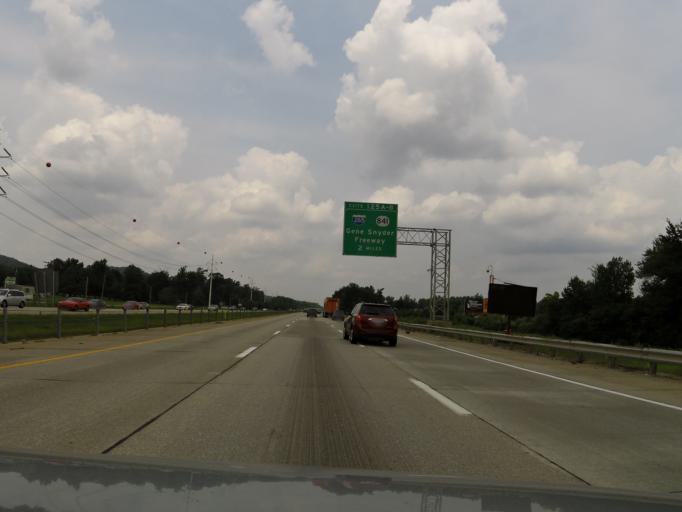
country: US
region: Kentucky
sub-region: Bullitt County
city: Hillview
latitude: 38.0807
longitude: -85.7005
